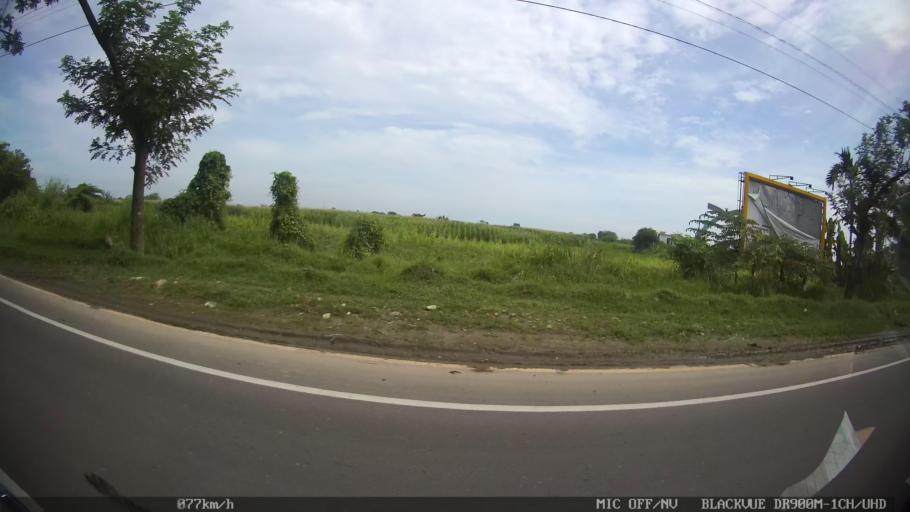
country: ID
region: North Sumatra
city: Percut
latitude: 3.5991
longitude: 98.8193
